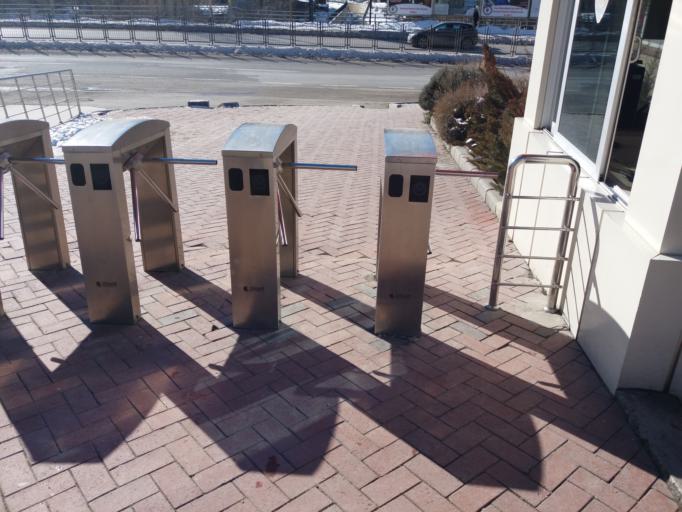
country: TR
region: Gumushane
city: Gumushkhane
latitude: 40.4359
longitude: 39.5148
